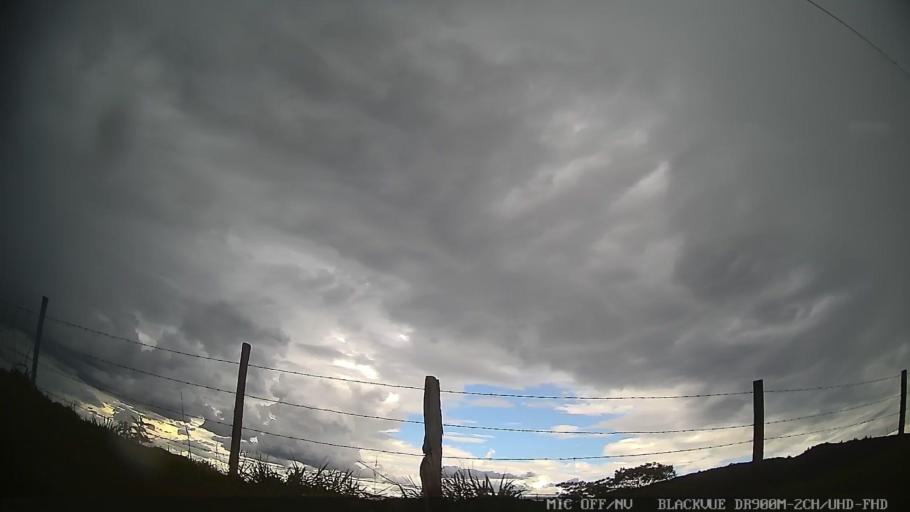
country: BR
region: Sao Paulo
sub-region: Pedreira
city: Pedreira
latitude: -22.7063
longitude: -46.8871
